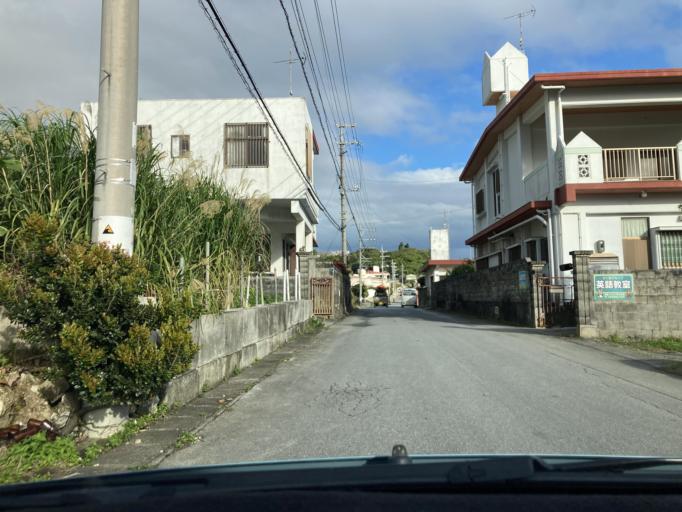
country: JP
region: Okinawa
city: Itoman
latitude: 26.1168
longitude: 127.6707
